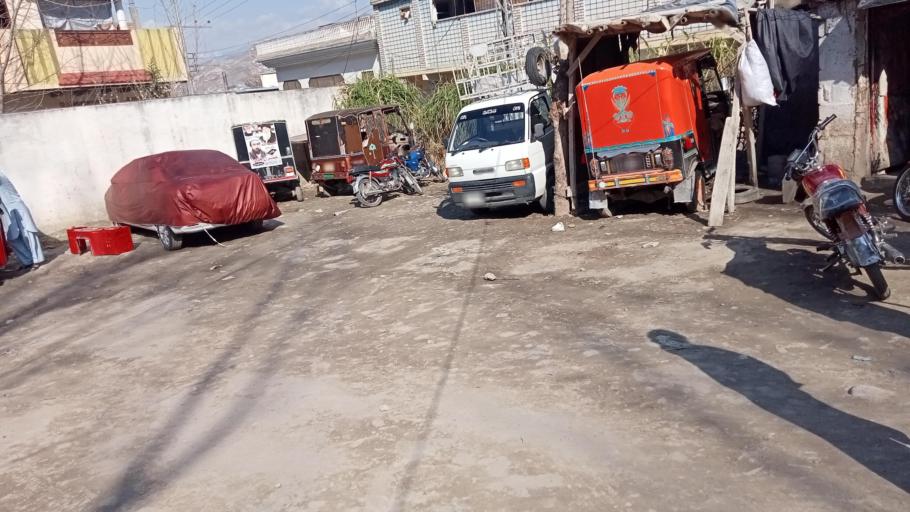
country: PK
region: Khyber Pakhtunkhwa
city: Saidu Sharif
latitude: 34.7639
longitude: 72.3496
